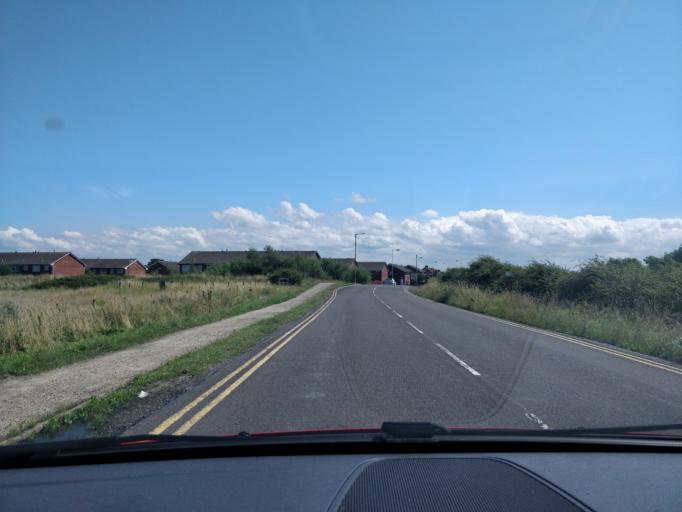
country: GB
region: England
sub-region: Sefton
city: Southport
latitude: 53.6730
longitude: -2.9764
